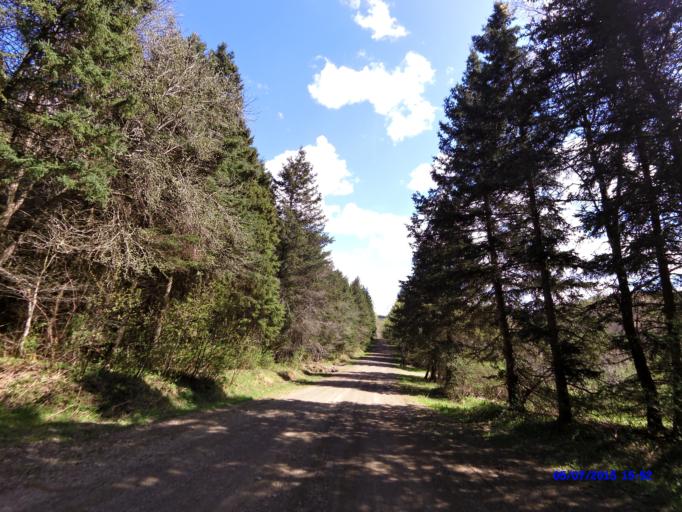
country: US
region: New York
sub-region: Cattaraugus County
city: Franklinville
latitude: 42.3280
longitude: -78.5425
